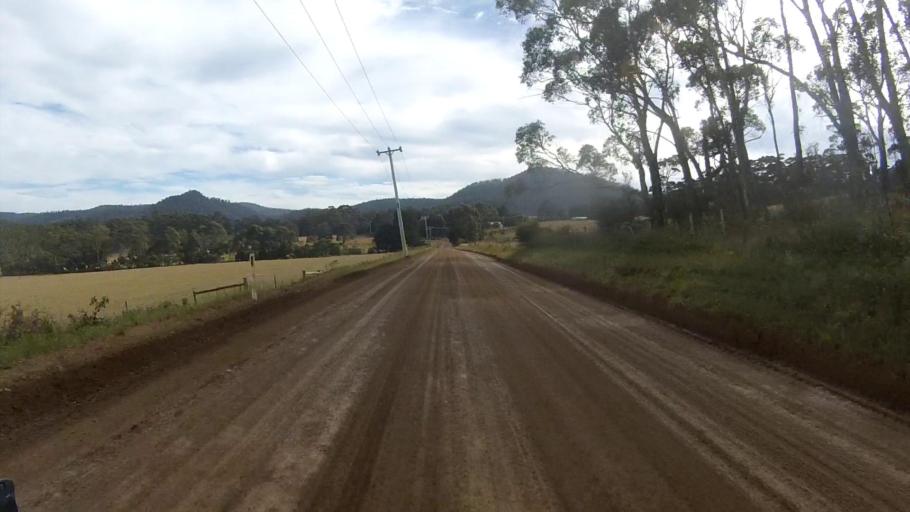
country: AU
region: Tasmania
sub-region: Sorell
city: Sorell
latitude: -42.7832
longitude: 147.8083
